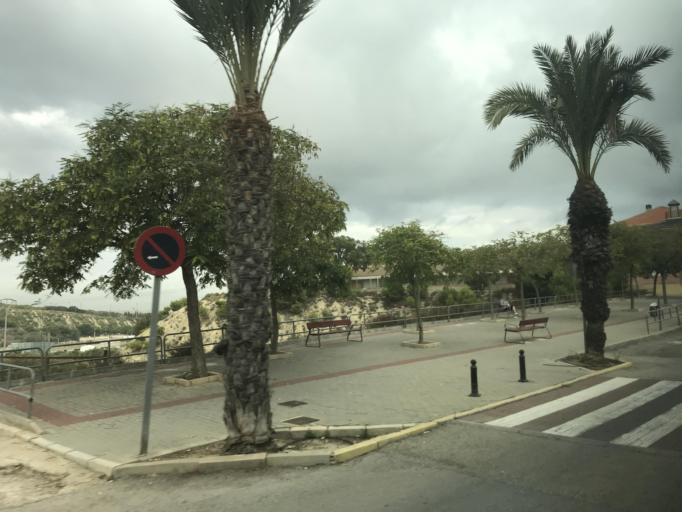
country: ES
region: Valencia
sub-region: Provincia de Alicante
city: Guardamar del Segura
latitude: 38.0854
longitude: -0.6554
